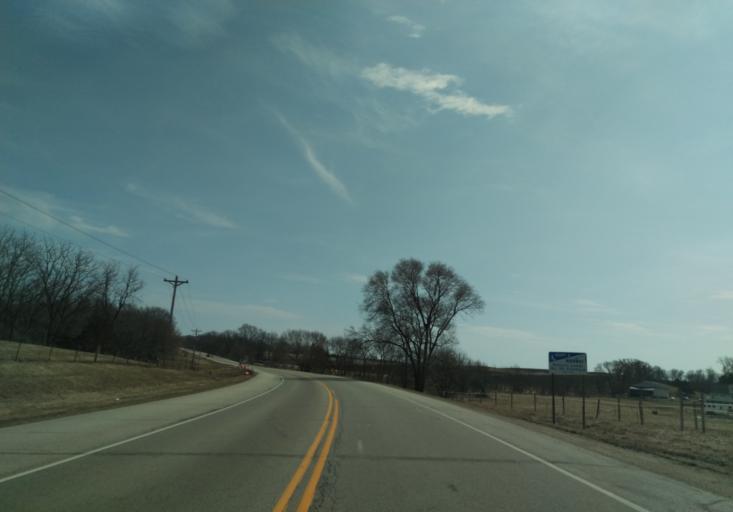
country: US
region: Minnesota
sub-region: Olmsted County
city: Eyota
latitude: 43.9390
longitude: -92.3483
